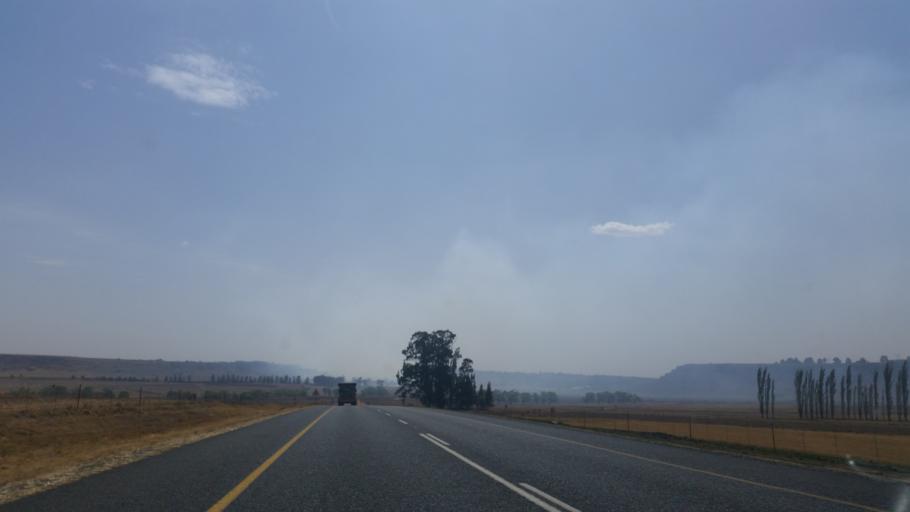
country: ZA
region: Orange Free State
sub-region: Thabo Mofutsanyana District Municipality
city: Bethlehem
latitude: -28.2766
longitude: 28.3812
